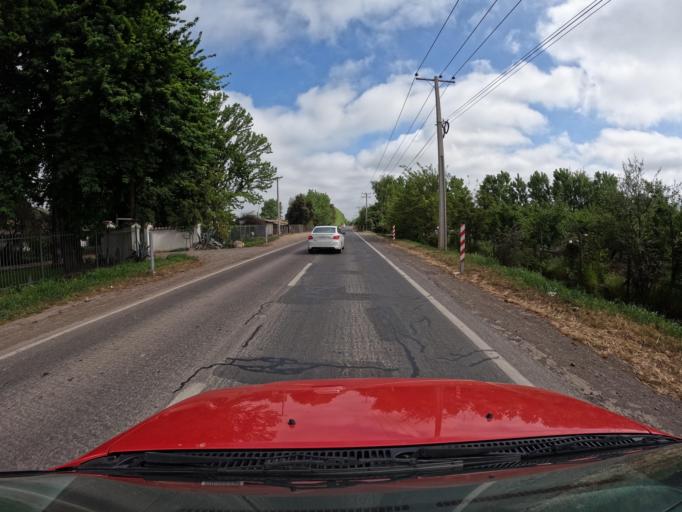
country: CL
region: O'Higgins
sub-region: Provincia de Colchagua
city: Santa Cruz
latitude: -34.7023
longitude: -71.3059
